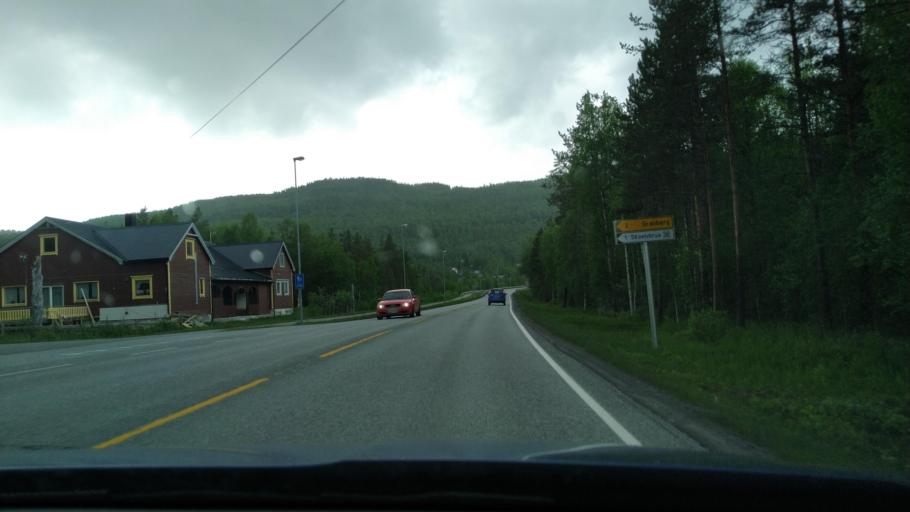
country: NO
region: Troms
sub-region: Malselv
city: Moen
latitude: 69.0095
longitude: 18.4954
